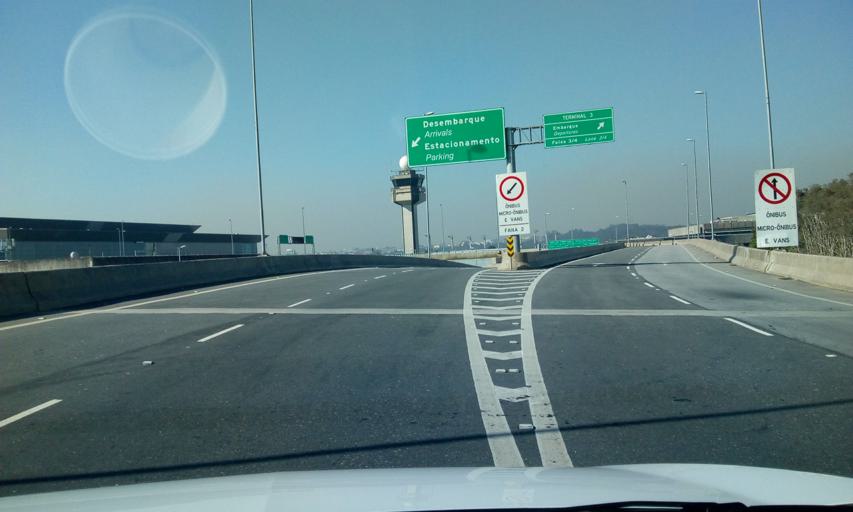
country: BR
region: Sao Paulo
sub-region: Guarulhos
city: Guarulhos
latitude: -23.4229
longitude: -46.4798
